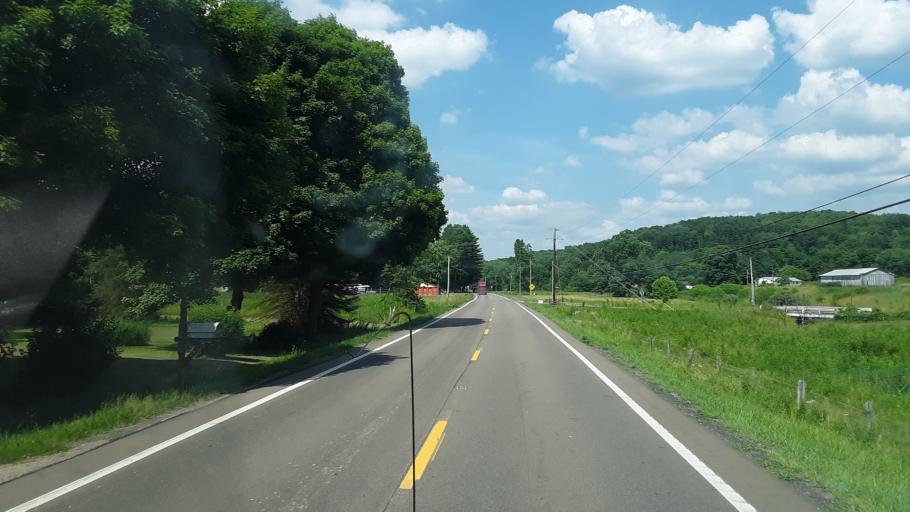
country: US
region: Ohio
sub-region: Tuscarawas County
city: Rockford
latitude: 40.5163
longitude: -81.2242
